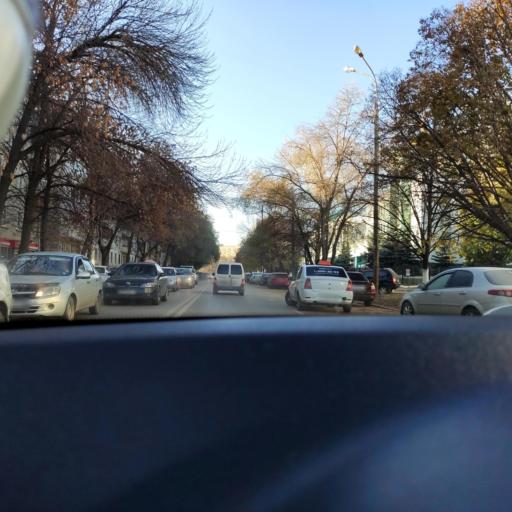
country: RU
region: Samara
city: Samara
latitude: 53.2090
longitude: 50.2307
